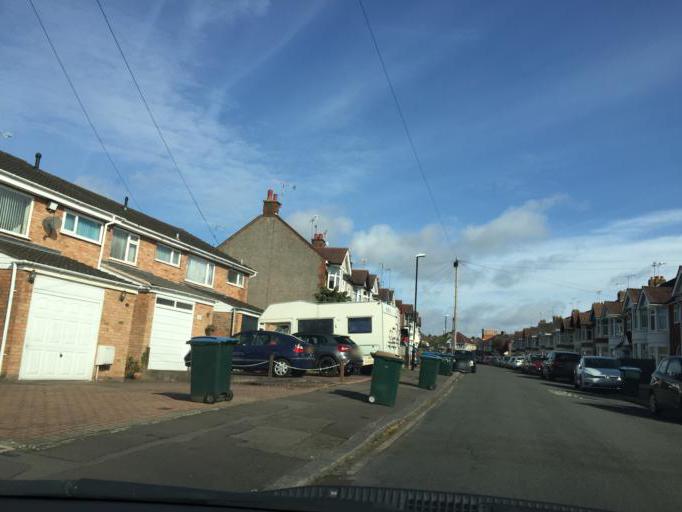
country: GB
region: England
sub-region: Coventry
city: Coventry
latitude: 52.3909
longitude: -1.4964
